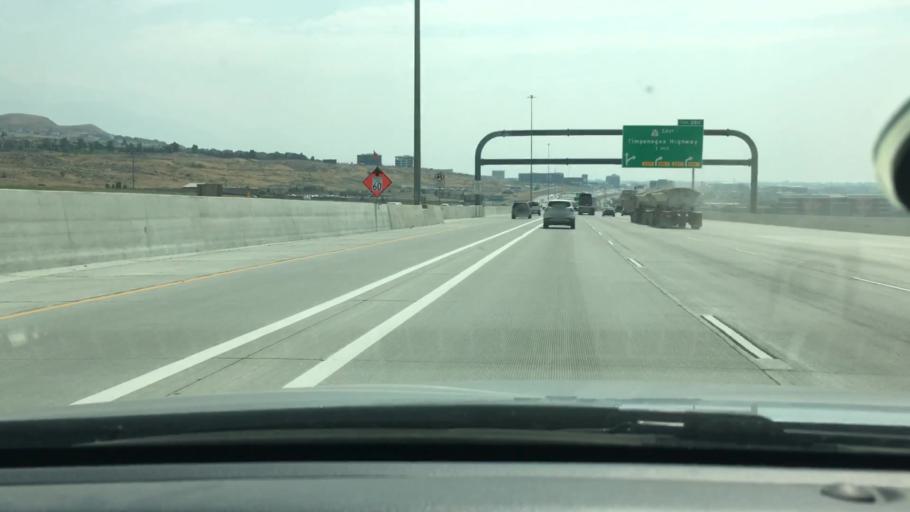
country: US
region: Utah
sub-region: Salt Lake County
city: Bluffdale
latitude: 40.4469
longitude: -111.9096
